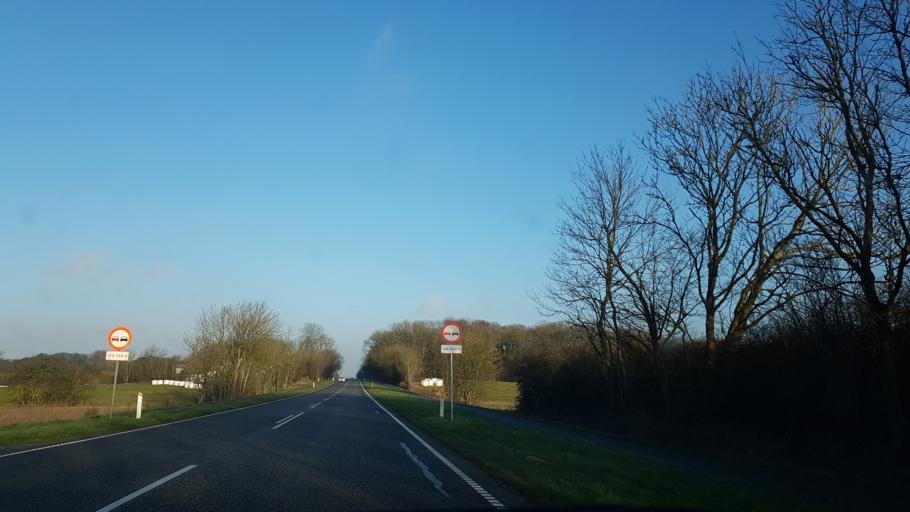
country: DK
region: South Denmark
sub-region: Haderslev Kommune
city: Haderslev
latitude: 55.2178
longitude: 9.4668
